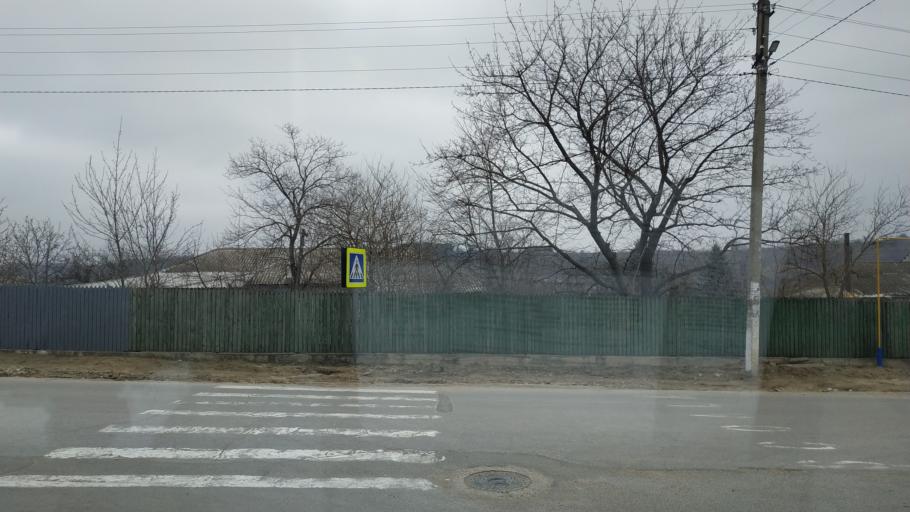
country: MD
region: Hincesti
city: Hincesti
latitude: 46.8876
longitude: 28.4119
